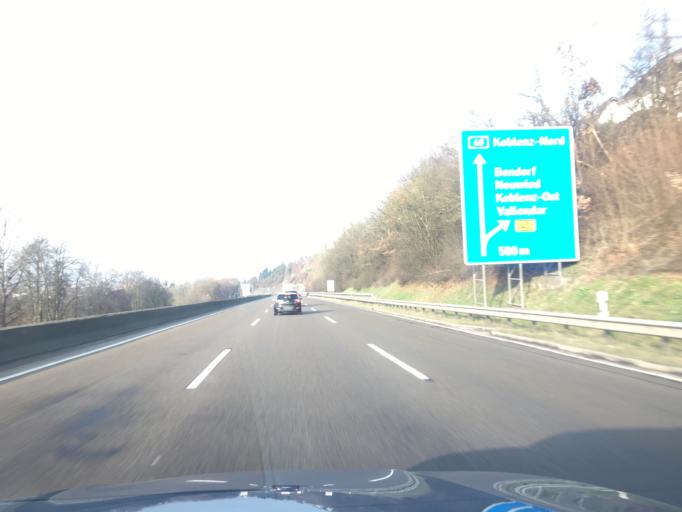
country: DE
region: Rheinland-Pfalz
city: Weitersburg
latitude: 50.4109
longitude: 7.5916
